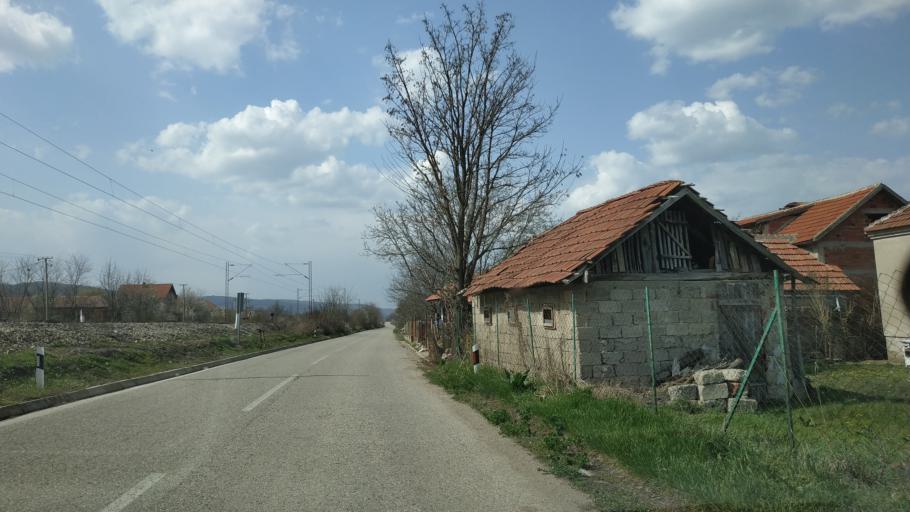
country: RS
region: Central Serbia
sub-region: Nisavski Okrug
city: Razanj
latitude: 43.5663
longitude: 21.5932
